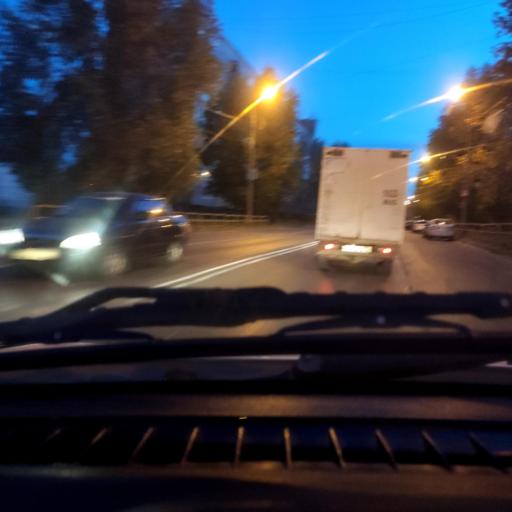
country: RU
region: Samara
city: Zhigulevsk
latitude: 53.4745
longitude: 49.5213
